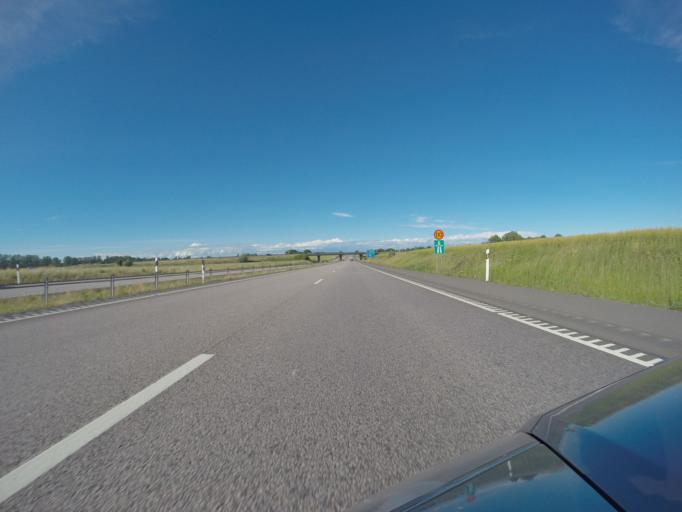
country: SE
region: Skane
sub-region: Helsingborg
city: Odakra
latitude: 56.0965
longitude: 12.7898
